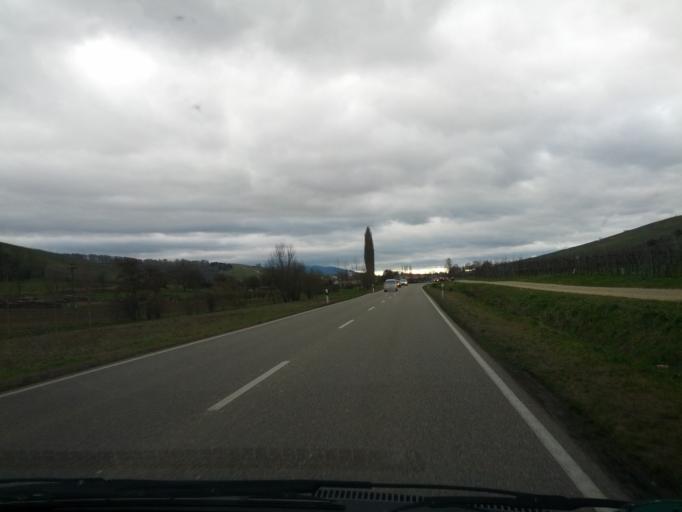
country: DE
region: Baden-Wuerttemberg
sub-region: Freiburg Region
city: Schallstadt
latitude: 47.9502
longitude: 7.7595
